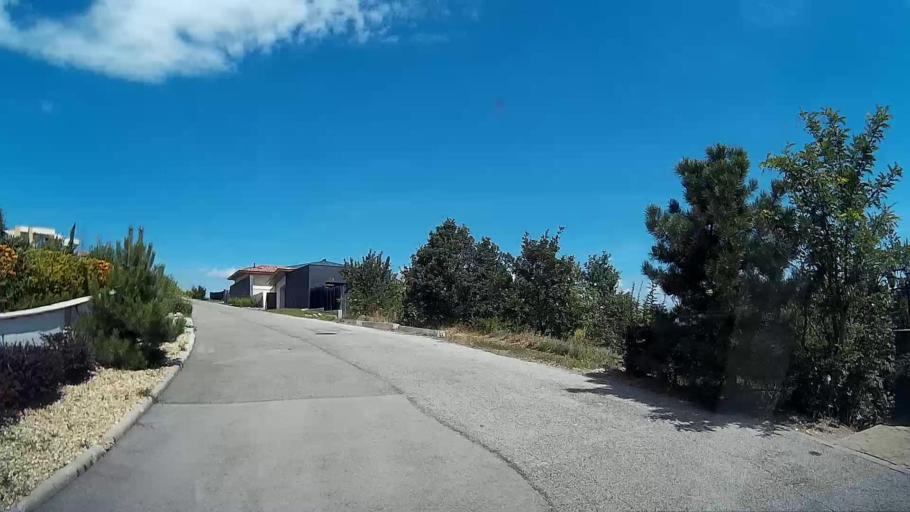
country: HU
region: Pest
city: Leanyfalu
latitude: 47.7034
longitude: 19.0765
